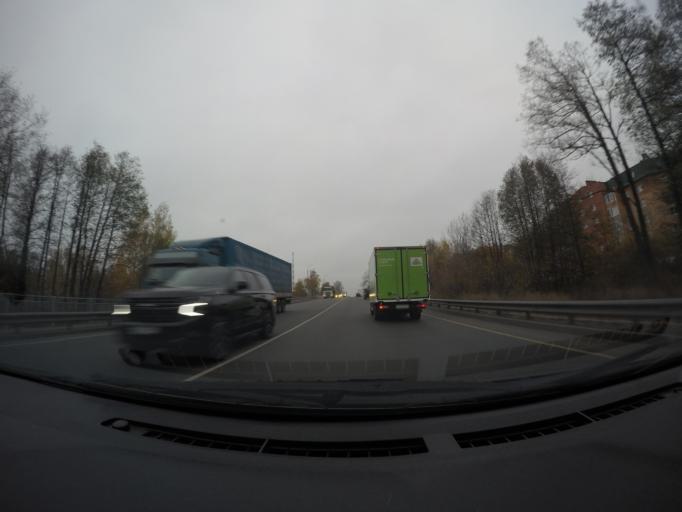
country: RU
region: Moskovskaya
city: Bronnitsy
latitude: 55.4149
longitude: 38.2592
